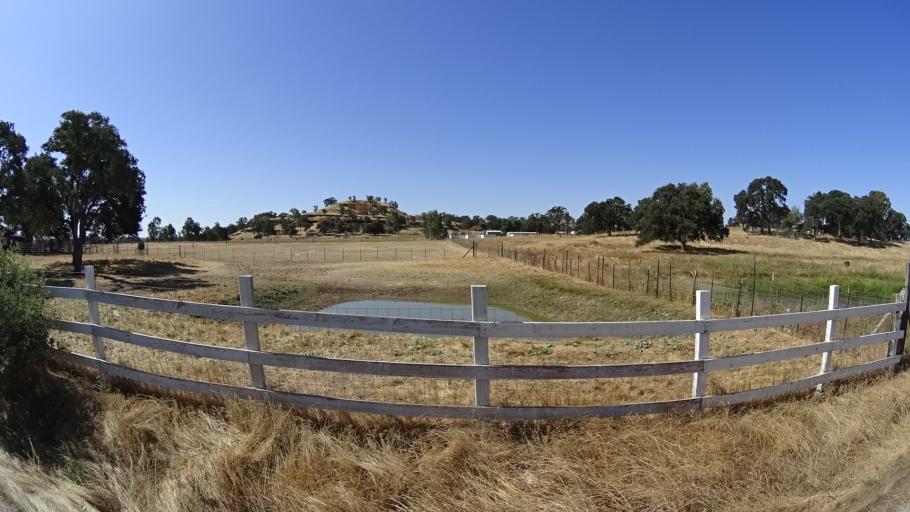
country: US
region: California
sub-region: Calaveras County
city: Rancho Calaveras
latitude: 38.0976
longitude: -120.8926
